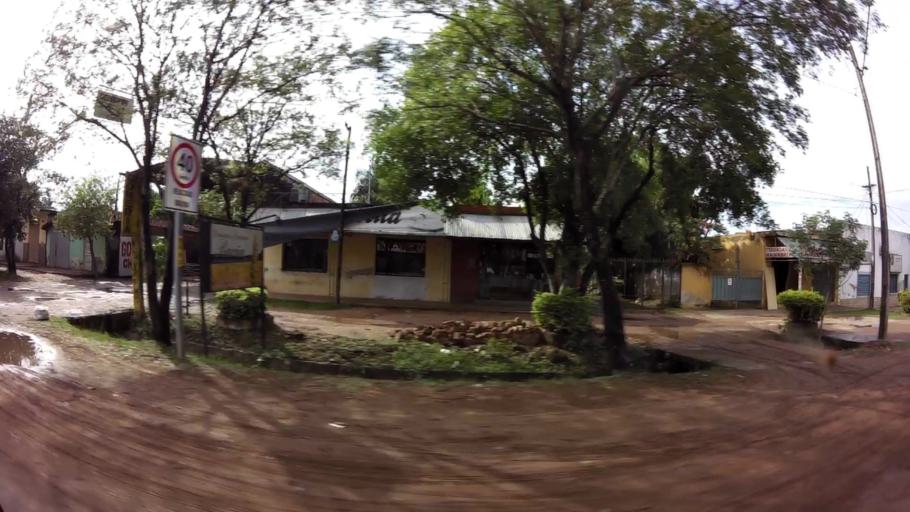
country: PY
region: Central
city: Limpio
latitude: -25.1702
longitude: -57.4795
